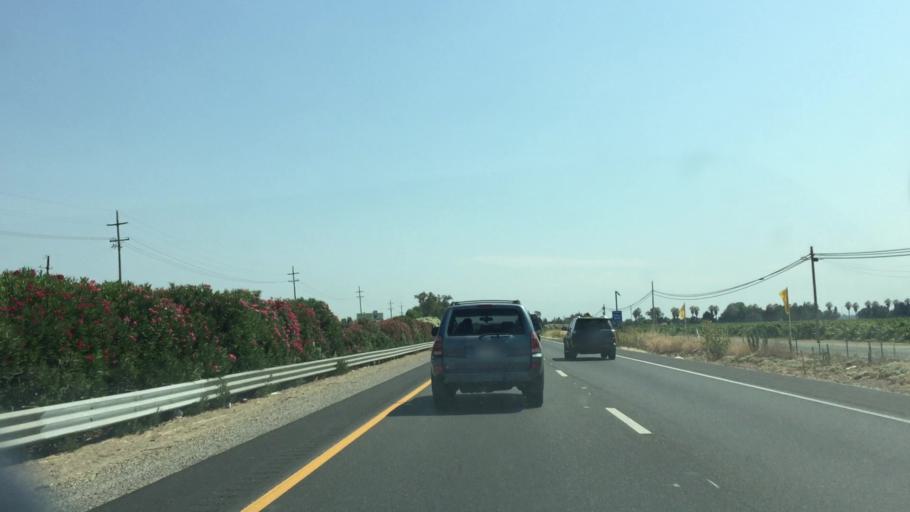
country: US
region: California
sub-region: San Joaquin County
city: Collierville
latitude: 38.1815
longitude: -121.2626
